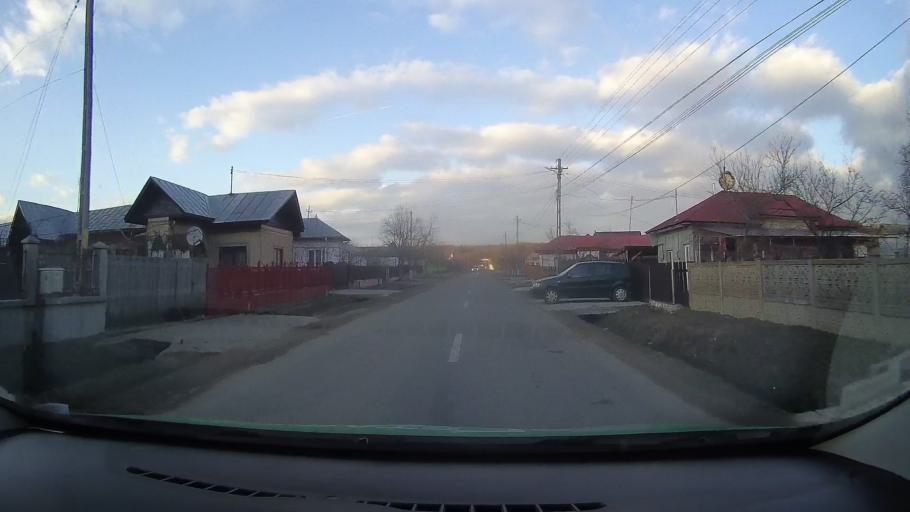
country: RO
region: Dambovita
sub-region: Comuna Gura Ocnitei
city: Adanca
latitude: 44.9135
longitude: 25.6149
